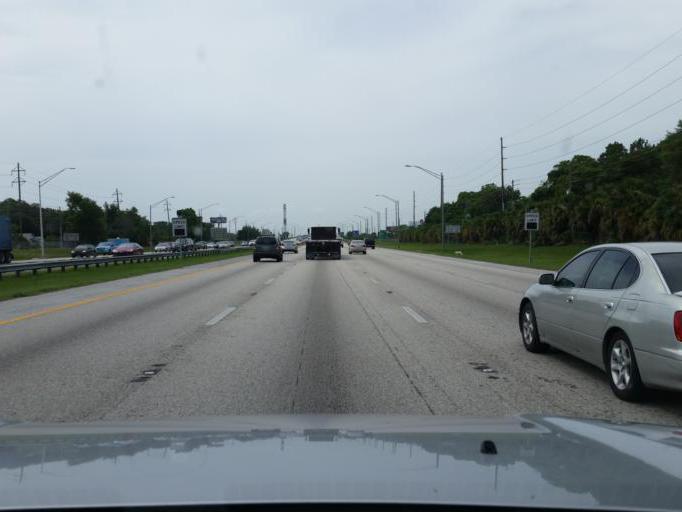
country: US
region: Florida
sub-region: Orange County
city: Eatonville
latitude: 28.6249
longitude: -81.3867
